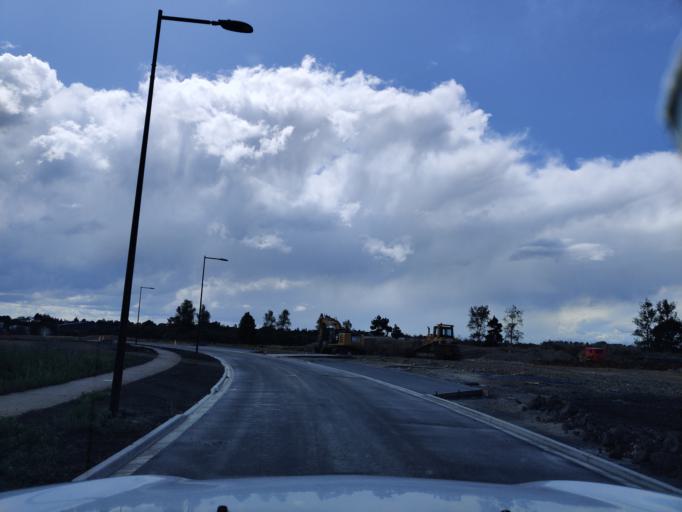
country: NZ
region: Waikato
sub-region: Waikato District
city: Te Kauwhata
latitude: -37.4111
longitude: 175.1531
